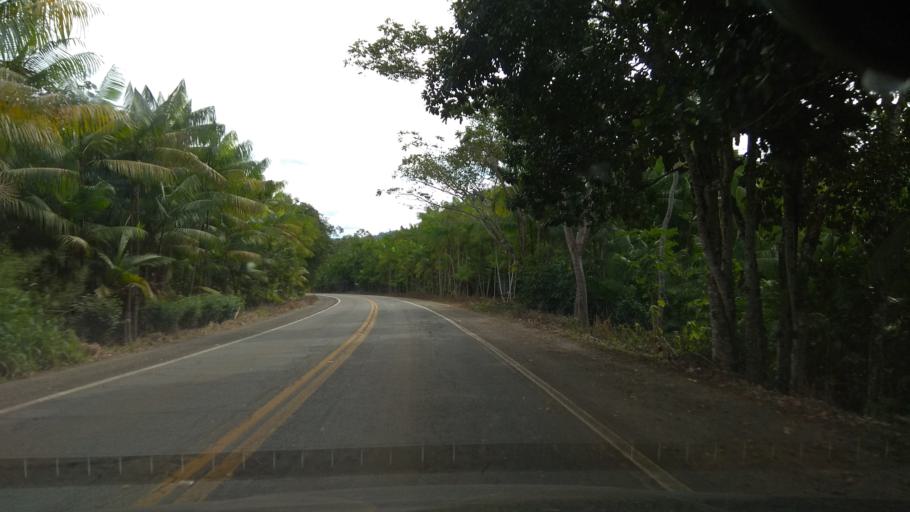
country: BR
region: Bahia
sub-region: Ubata
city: Ubata
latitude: -14.2295
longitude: -39.4373
